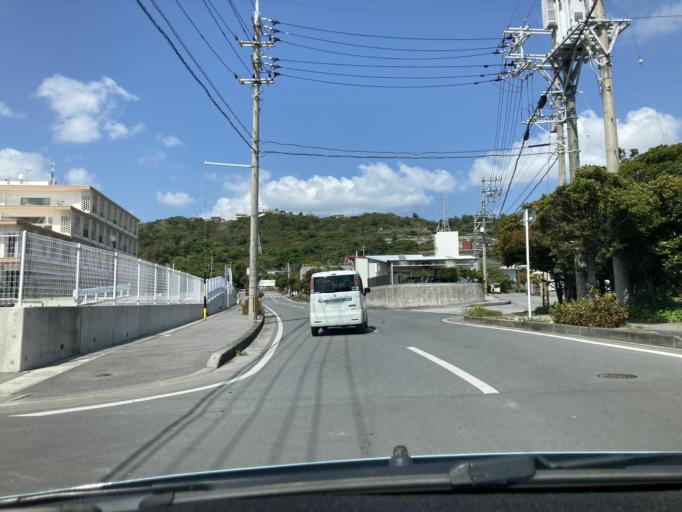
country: JP
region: Okinawa
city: Ginowan
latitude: 26.2620
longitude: 127.7907
